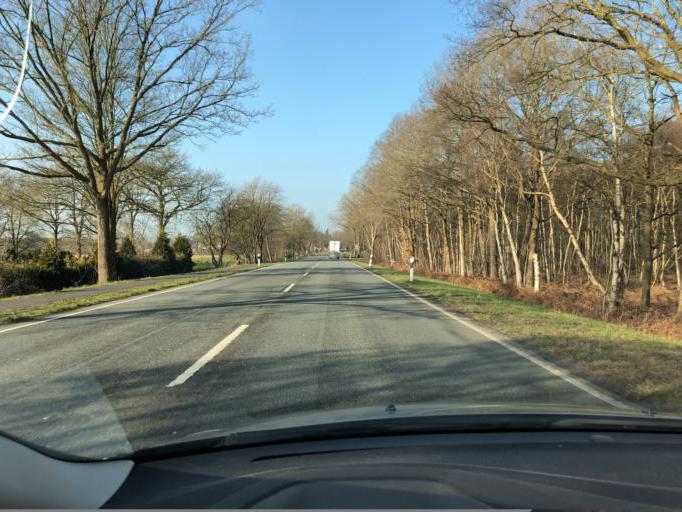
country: DE
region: Lower Saxony
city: Westerstede
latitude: 53.2917
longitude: 7.8808
